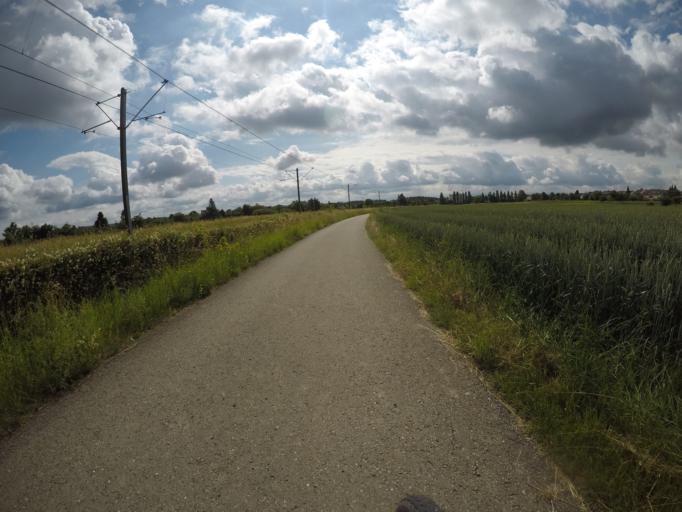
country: DE
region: Baden-Wuerttemberg
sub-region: Regierungsbezirk Stuttgart
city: Ostfildern
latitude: 48.7356
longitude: 9.2448
